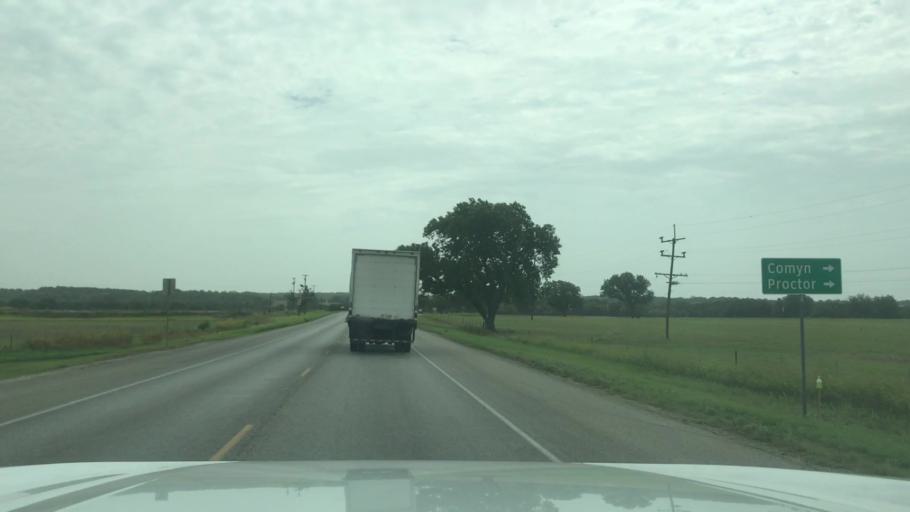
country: US
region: Texas
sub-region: Comanche County
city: De Leon
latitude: 32.0957
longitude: -98.4578
